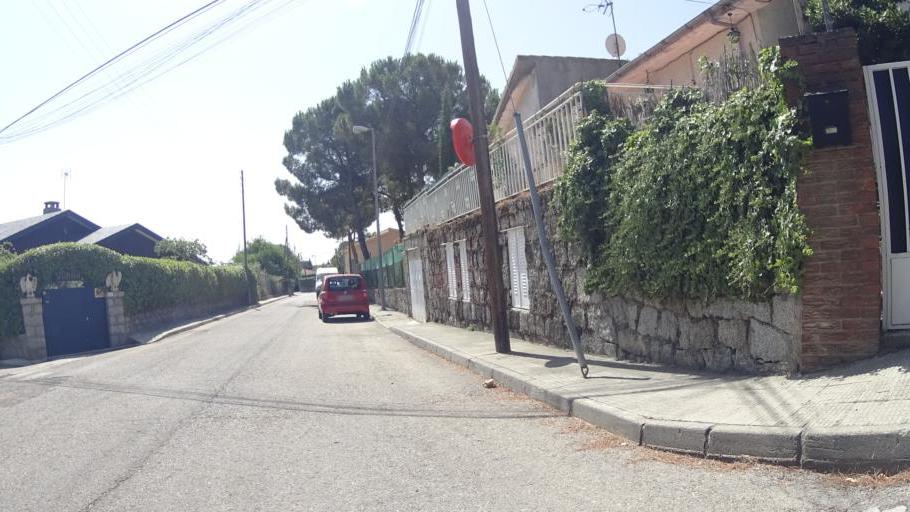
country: ES
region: Madrid
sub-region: Provincia de Madrid
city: Colmenarejo
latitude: 40.5595
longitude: -4.0097
